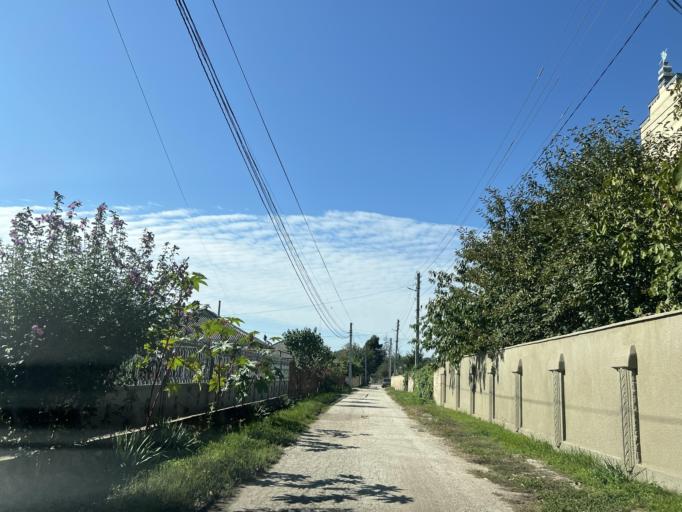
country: RO
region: Iasi
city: Ungheni-Prut
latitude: 47.1951
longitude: 27.7936
